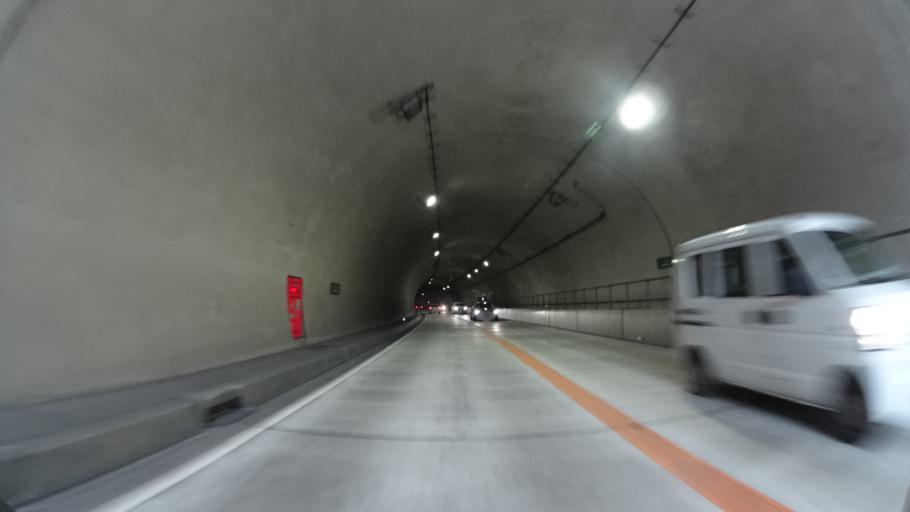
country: JP
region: Mie
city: Ueno-ebisumachi
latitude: 34.7747
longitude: 135.9957
